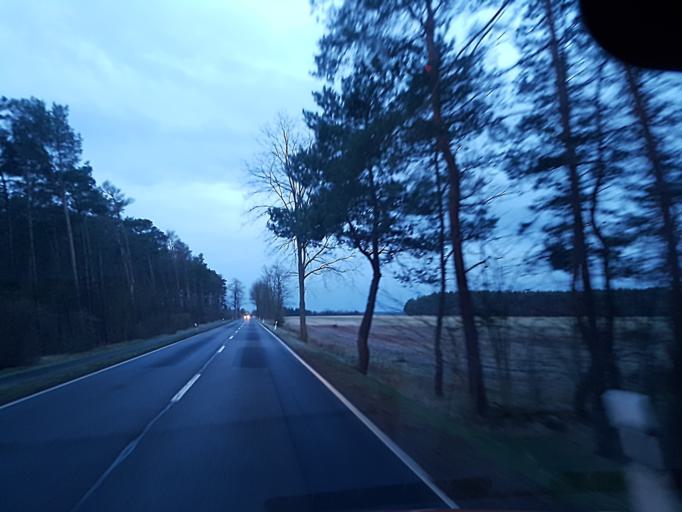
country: DE
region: Brandenburg
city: Finsterwalde
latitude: 51.5763
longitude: 13.6884
